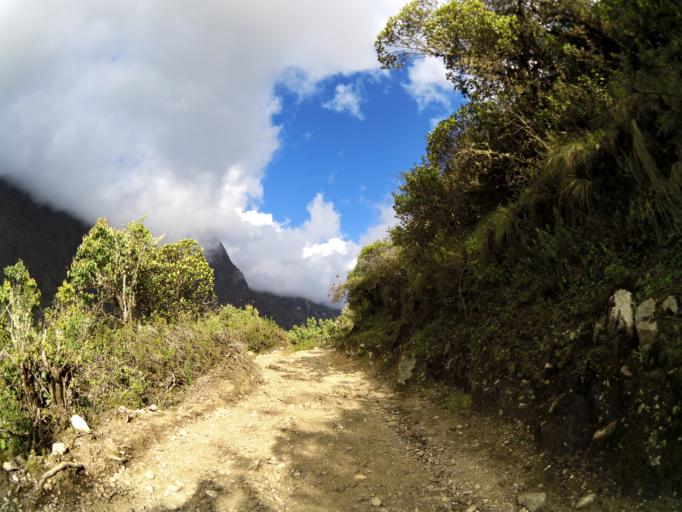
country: PE
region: Cusco
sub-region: Provincia de La Convencion
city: Santa Teresa
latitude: -13.3145
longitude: -72.6263
